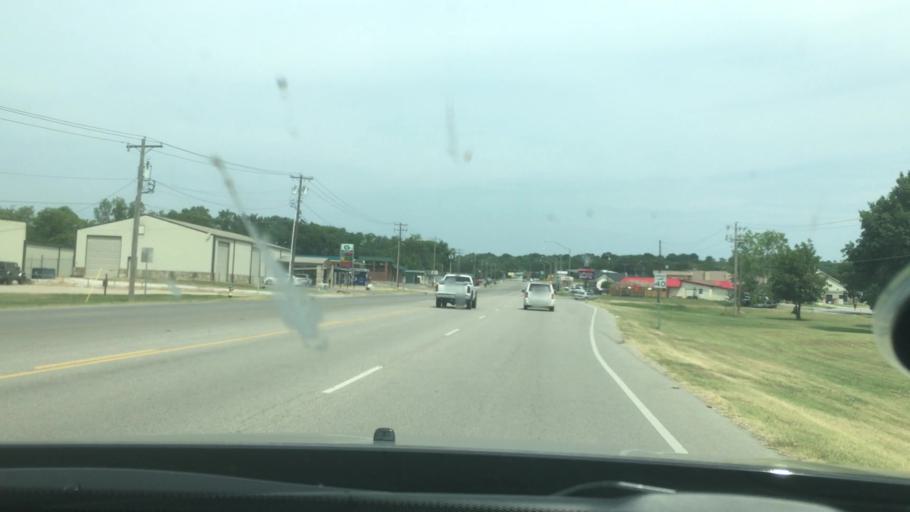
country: US
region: Oklahoma
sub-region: Pontotoc County
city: Ada
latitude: 34.7578
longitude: -96.6606
